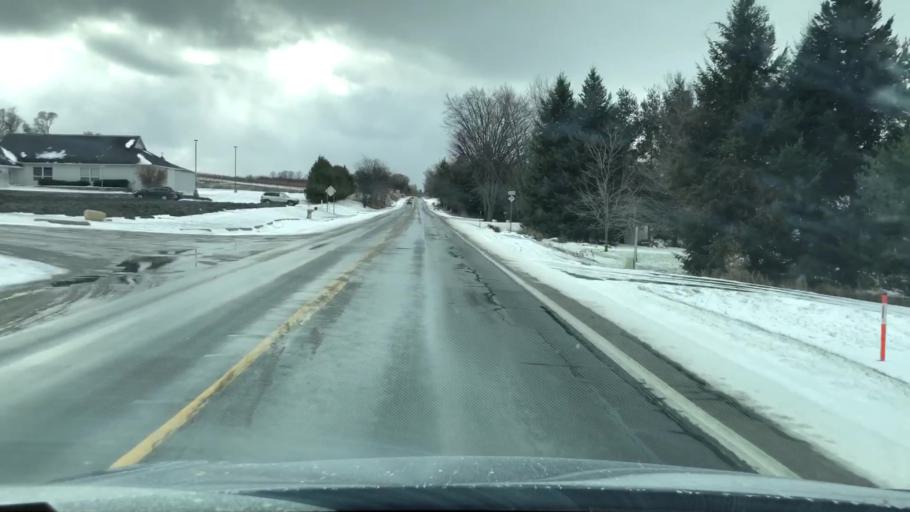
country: US
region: Michigan
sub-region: Antrim County
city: Elk Rapids
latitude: 44.8840
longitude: -85.5154
